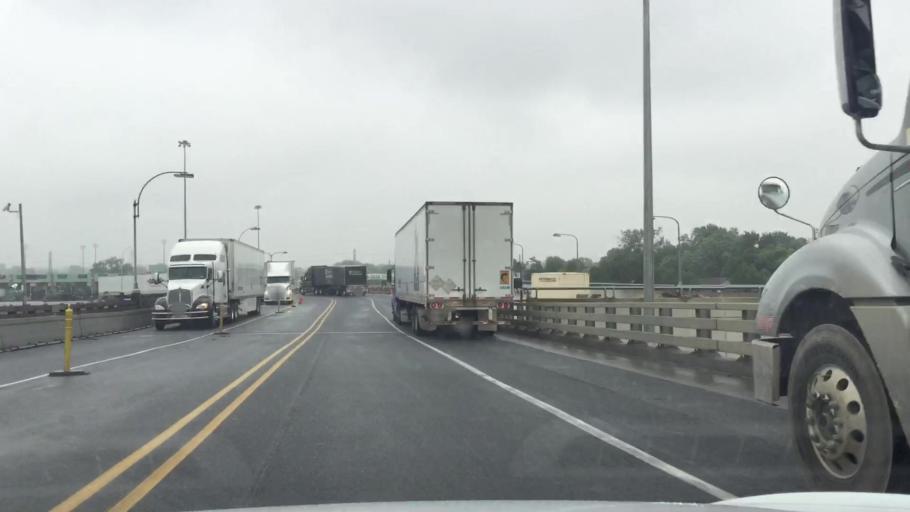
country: US
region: Michigan
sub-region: Wayne County
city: Detroit
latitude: 42.3034
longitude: -83.0685
